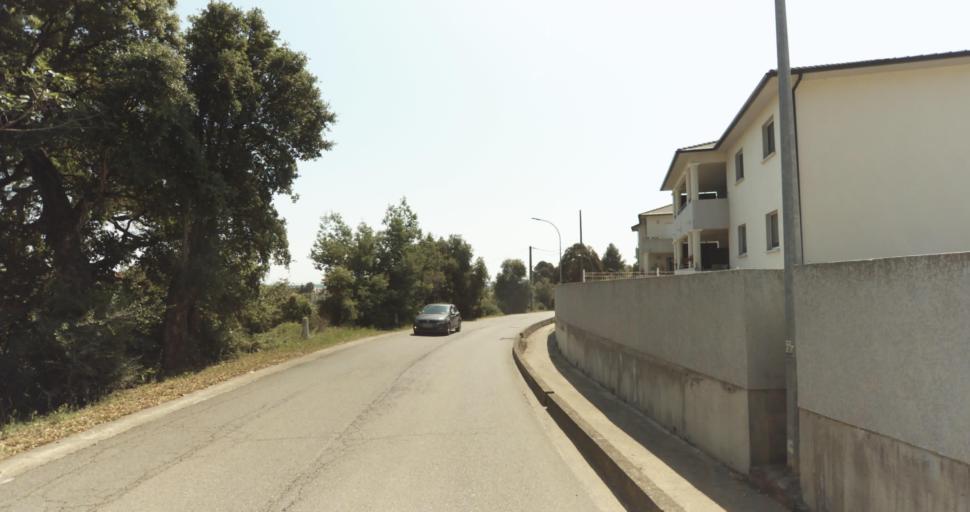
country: FR
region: Corsica
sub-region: Departement de la Haute-Corse
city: Biguglia
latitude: 42.6202
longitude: 9.4305
